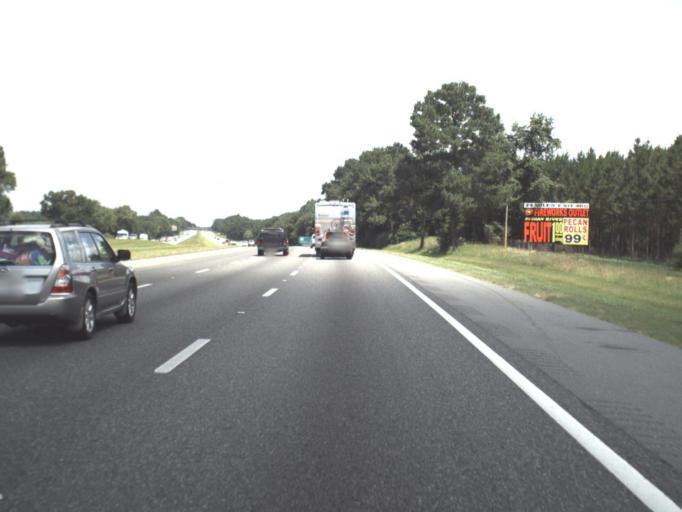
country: US
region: Florida
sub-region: Suwannee County
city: Wellborn
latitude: 30.2778
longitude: -82.7608
